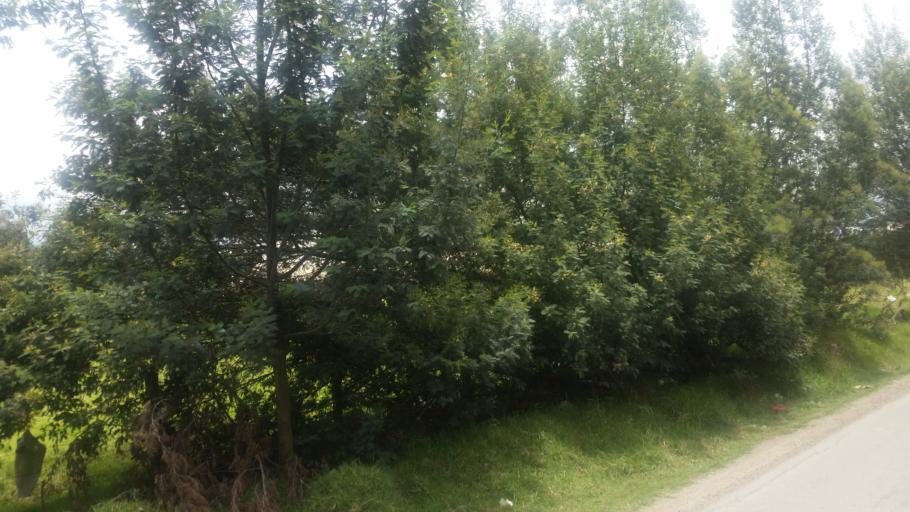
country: CO
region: Cundinamarca
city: Cogua
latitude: 5.0330
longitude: -73.9699
